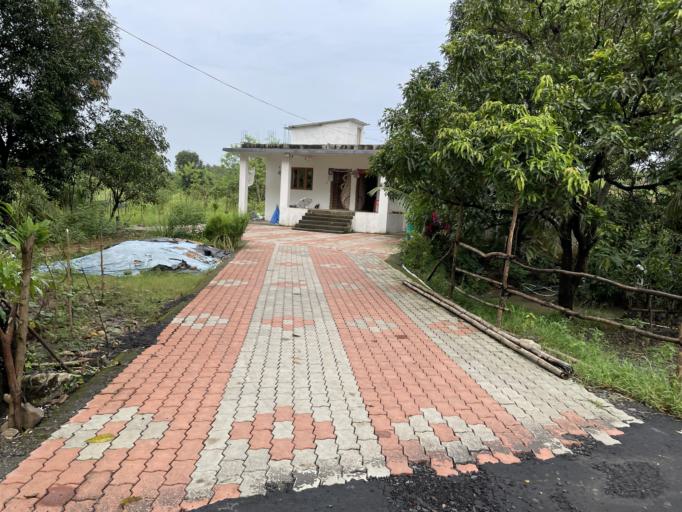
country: IN
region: Gujarat
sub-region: Valsad
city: Pardi
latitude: 20.4521
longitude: 72.9347
